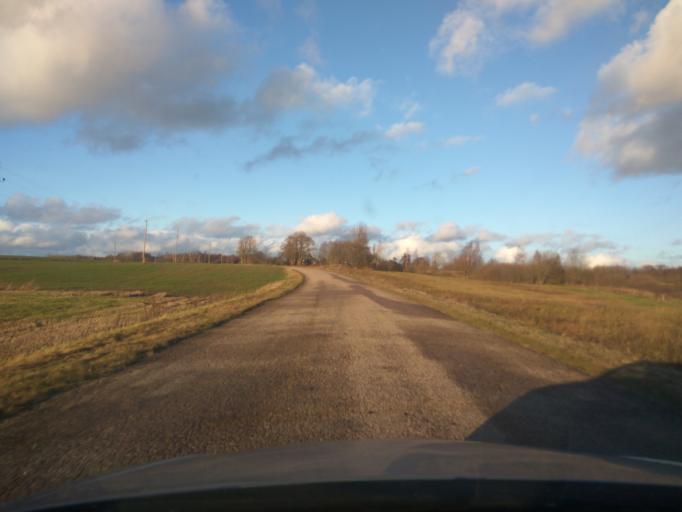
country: LV
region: Aizpute
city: Aizpute
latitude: 56.7681
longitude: 21.7844
